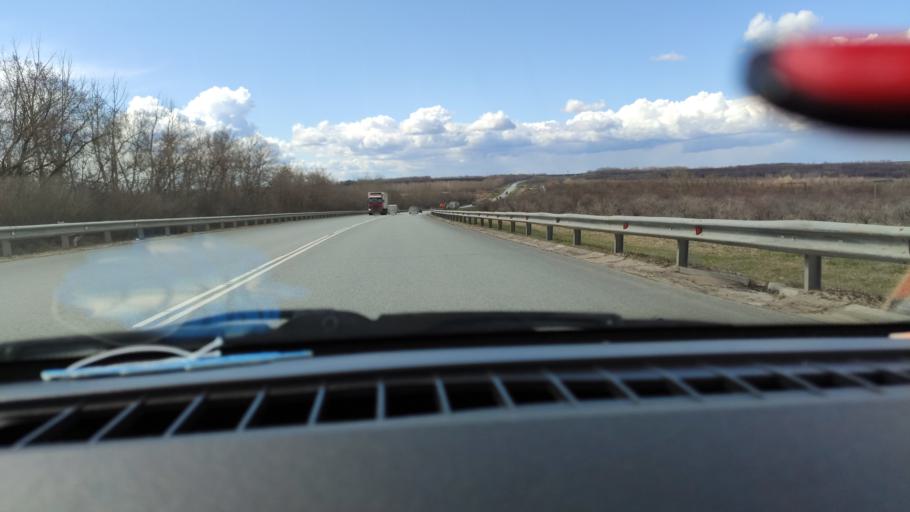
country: RU
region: Samara
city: Obsharovka
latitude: 53.2086
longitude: 48.8060
